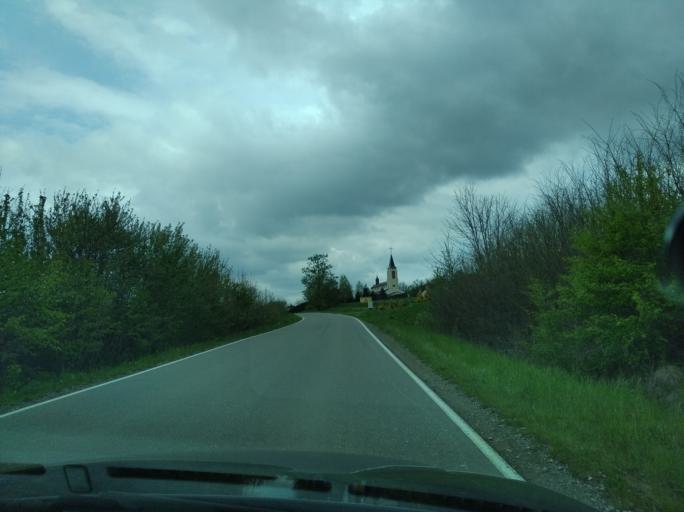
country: PL
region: Subcarpathian Voivodeship
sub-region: Powiat brzozowski
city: Turze Pole
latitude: 49.6372
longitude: 22.0030
